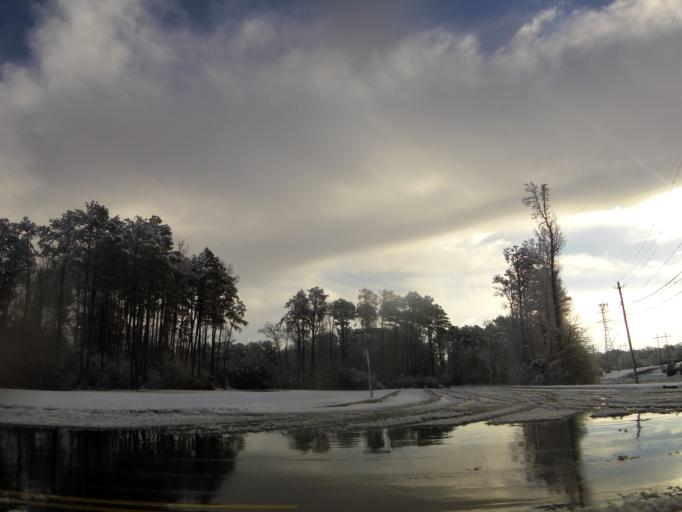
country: US
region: North Carolina
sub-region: Nash County
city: Rocky Mount
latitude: 35.9484
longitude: -77.8477
